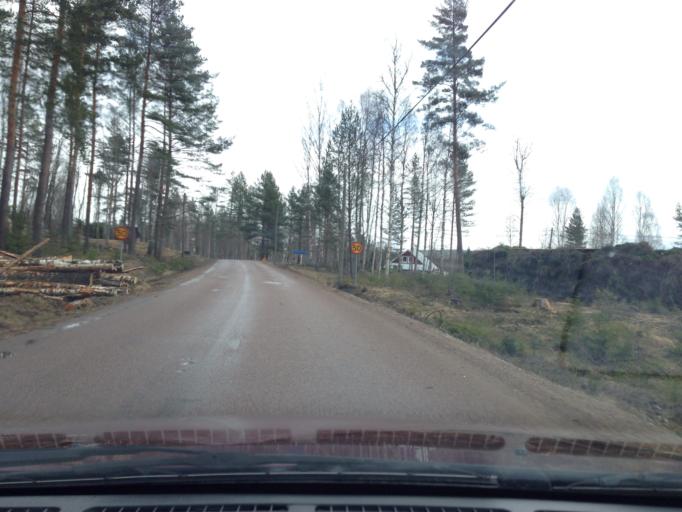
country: SE
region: Dalarna
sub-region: Ludvika Kommun
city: Ludvika
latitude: 60.1745
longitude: 15.2838
